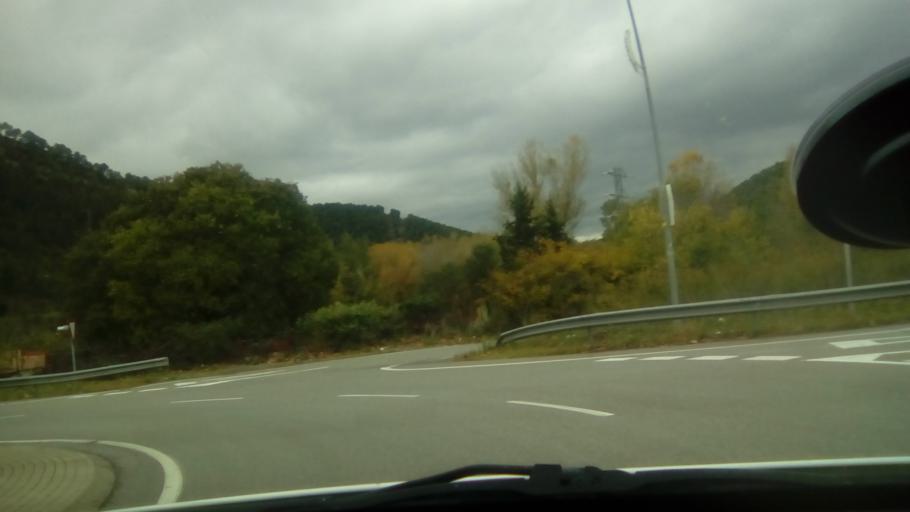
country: ES
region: Catalonia
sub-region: Provincia de Barcelona
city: Sant Fruitos de Bages
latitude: 41.7044
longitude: 1.8711
